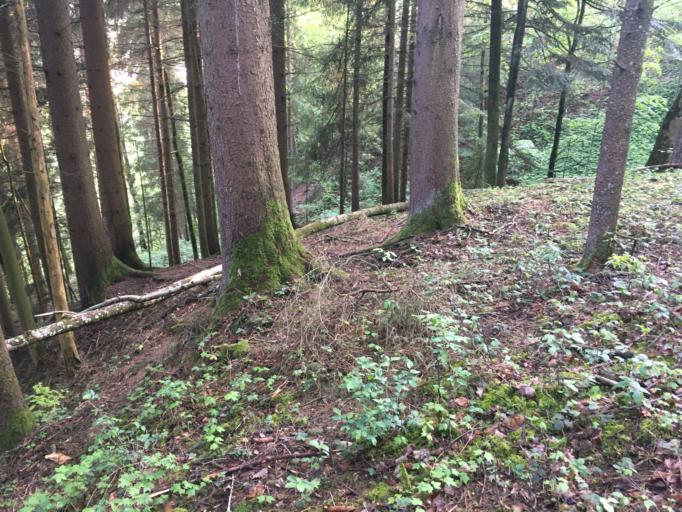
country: AT
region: Upper Austria
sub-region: Politischer Bezirk Vocklabruck
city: Vocklamarkt
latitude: 48.0086
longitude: 13.4938
